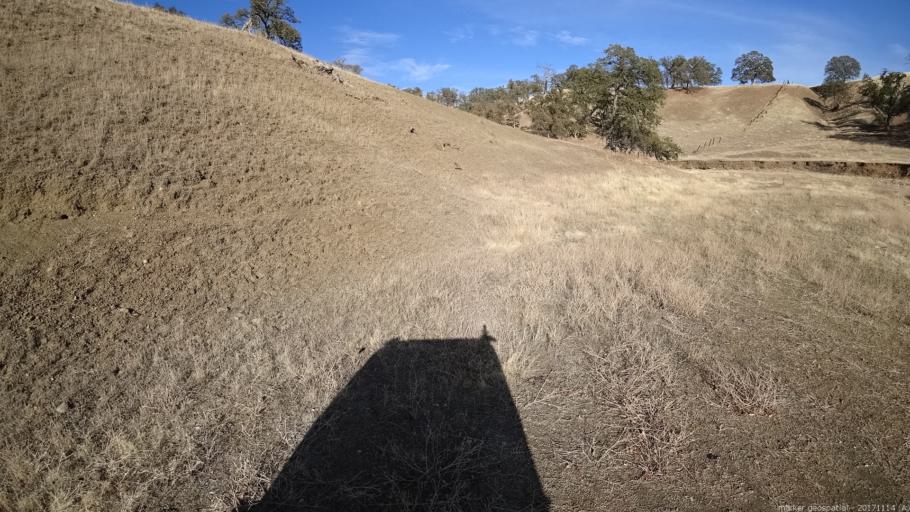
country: US
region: California
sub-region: Shasta County
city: Shasta
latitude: 40.3696
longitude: -122.5770
